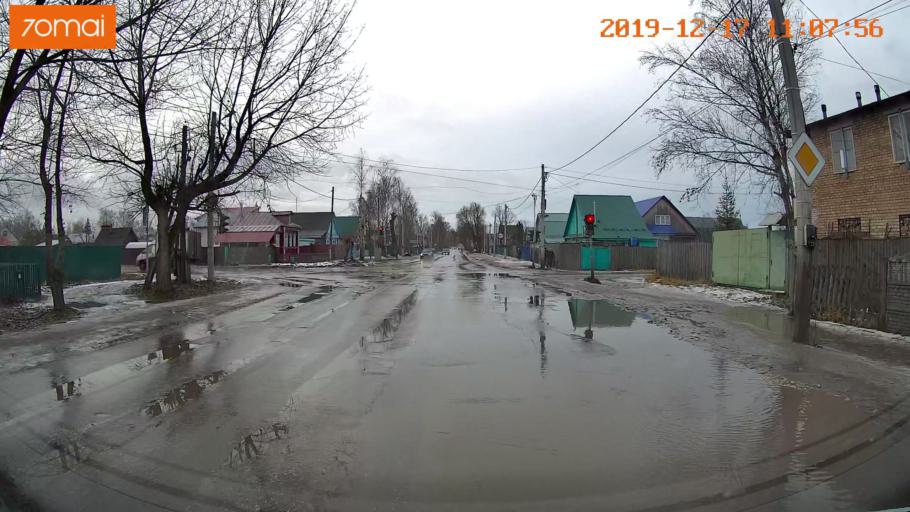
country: RU
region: Vladimir
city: Gus'-Khrustal'nyy
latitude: 55.6081
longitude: 40.6433
